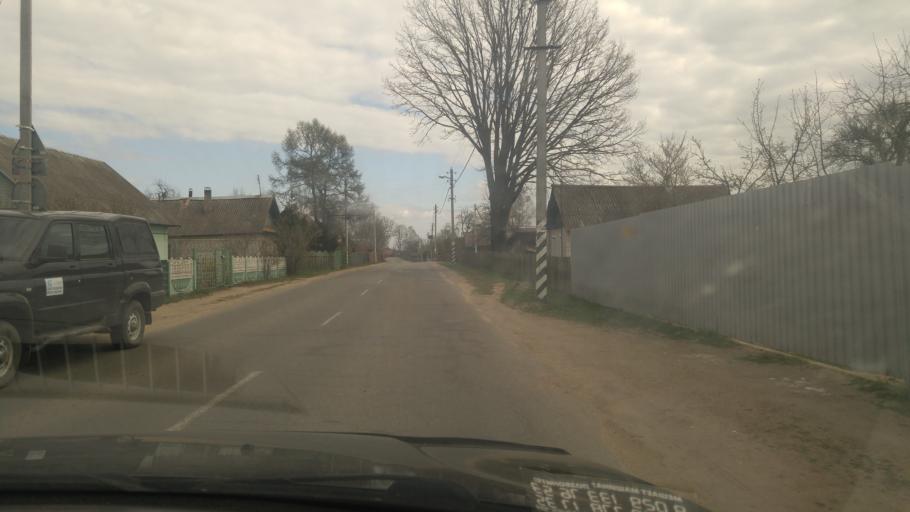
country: BY
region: Minsk
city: Rudzyensk
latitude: 53.6595
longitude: 27.7814
